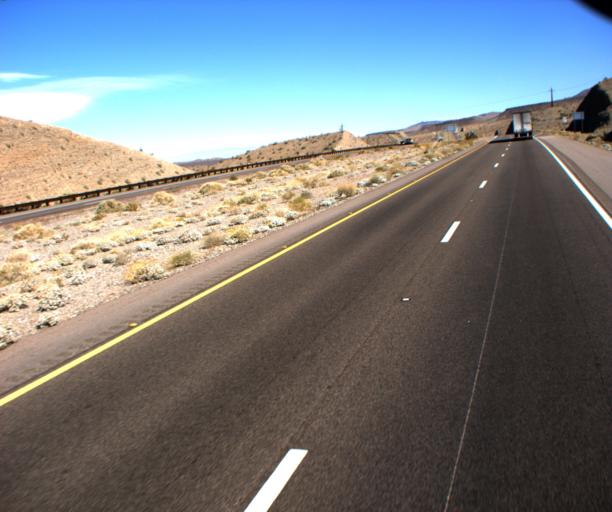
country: US
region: Nevada
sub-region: Clark County
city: Boulder City
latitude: 35.9130
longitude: -114.6288
